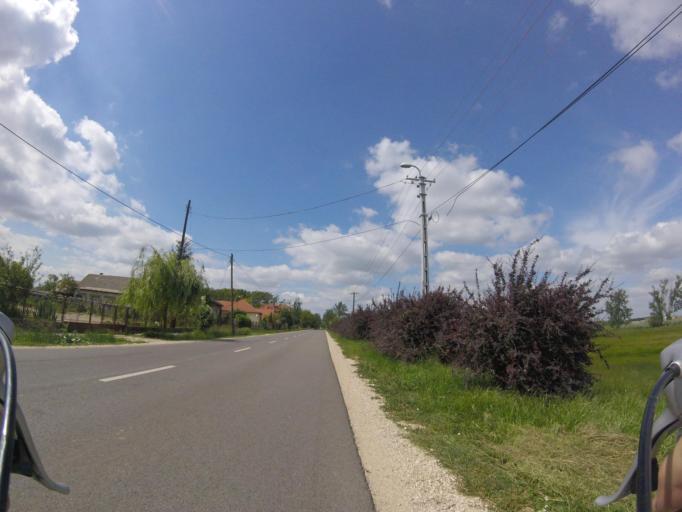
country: HU
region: Fejer
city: Soponya
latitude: 47.0279
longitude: 18.4441
